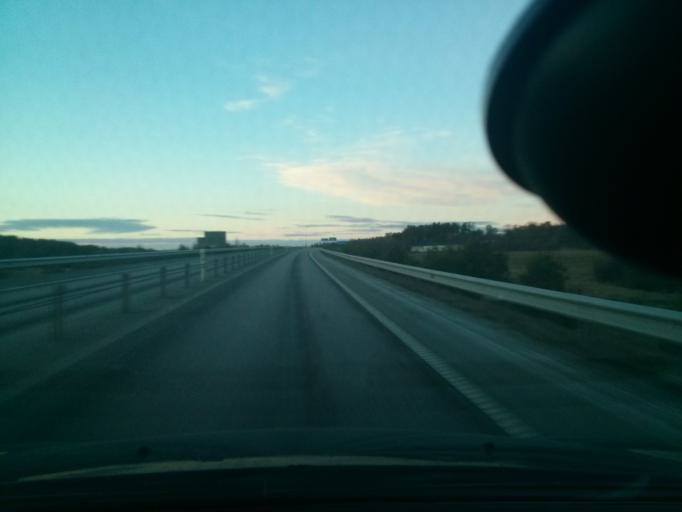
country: SE
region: Blekinge
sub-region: Ronneby Kommun
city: Kallinge
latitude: 56.2477
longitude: 15.2484
